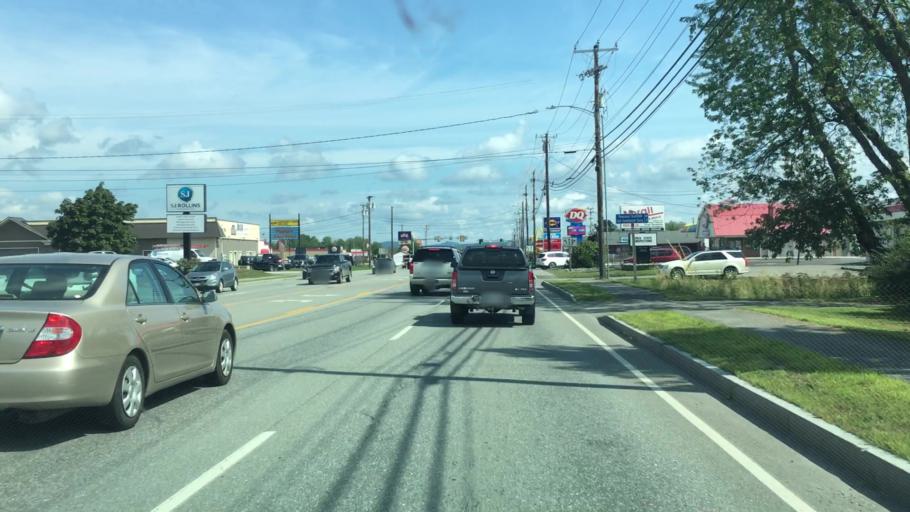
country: US
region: Maine
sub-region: Penobscot County
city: Brewer
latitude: 44.7815
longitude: -68.7454
